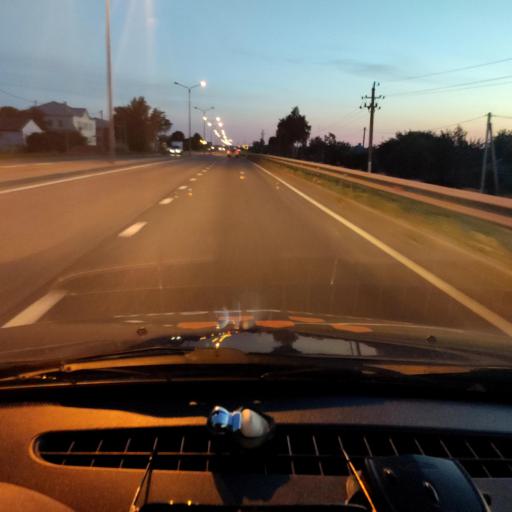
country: RU
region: Belgorod
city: Gubkin
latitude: 51.2636
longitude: 37.5454
